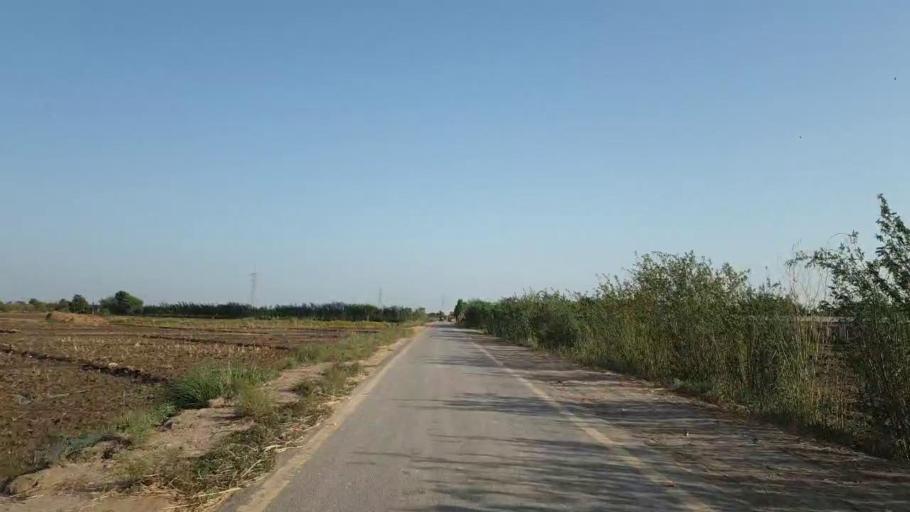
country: PK
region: Sindh
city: Hyderabad
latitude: 25.3530
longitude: 68.4126
